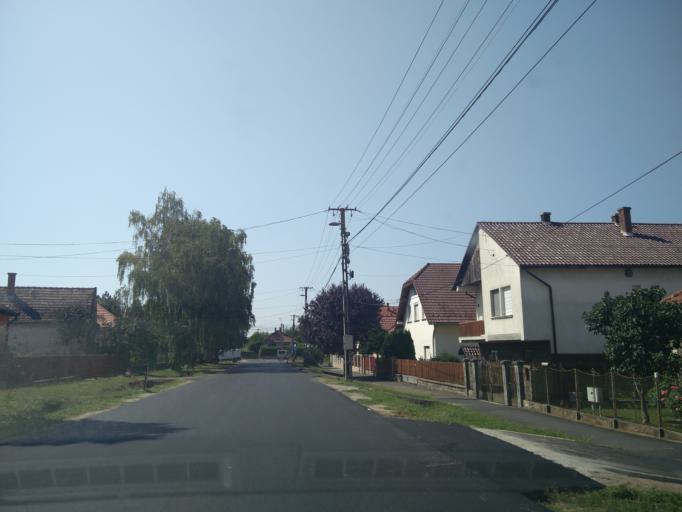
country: HU
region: Zala
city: Zalaegerszeg
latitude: 46.8432
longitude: 16.8767
